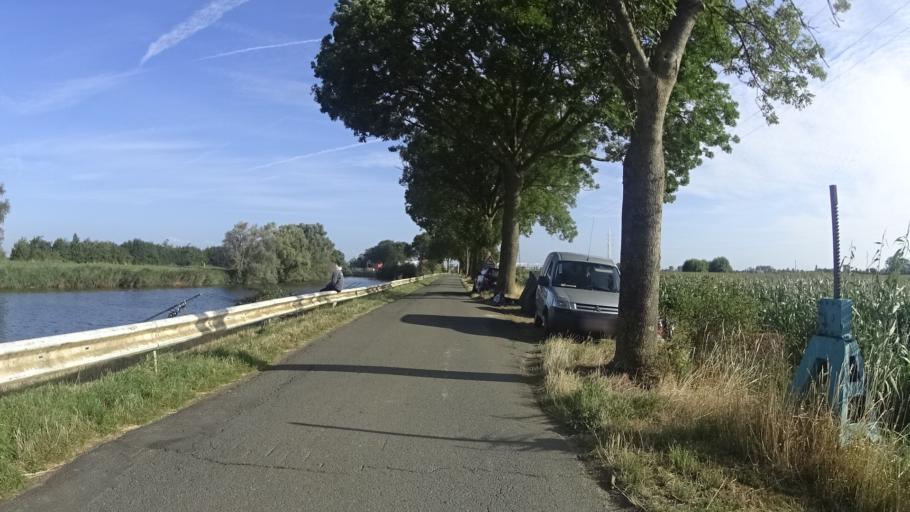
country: BE
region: Flanders
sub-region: Provincie West-Vlaanderen
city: Diksmuide
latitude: 50.9531
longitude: 2.8283
